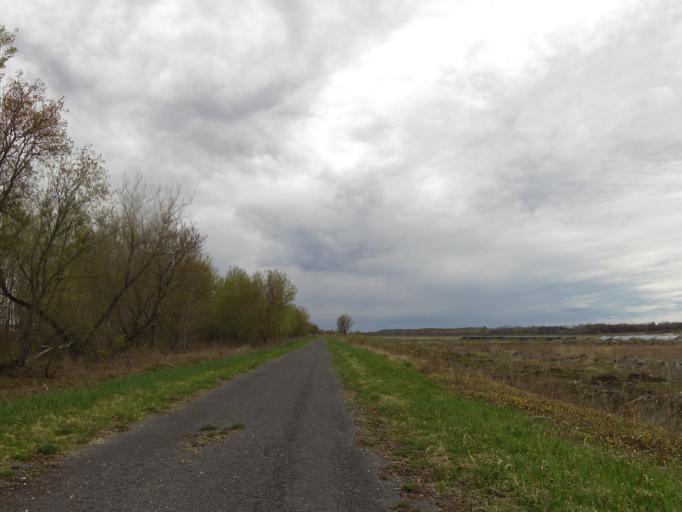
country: CA
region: Quebec
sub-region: Outaouais
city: Papineauville
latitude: 45.5331
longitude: -74.8849
